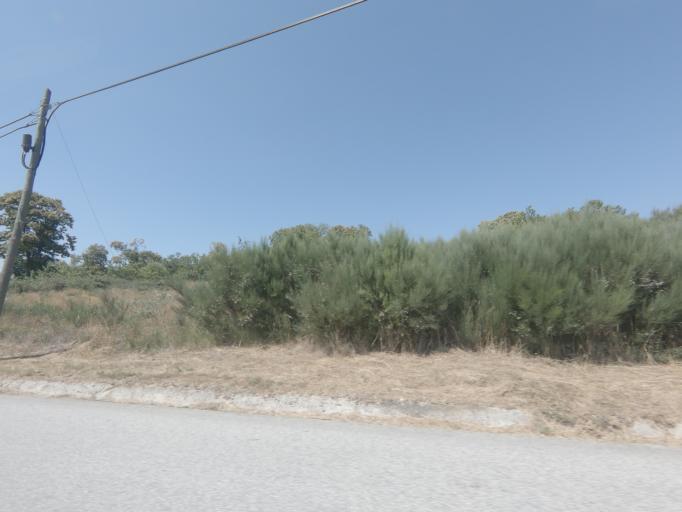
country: PT
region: Viseu
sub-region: Tarouca
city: Tarouca
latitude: 40.9920
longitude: -7.8164
